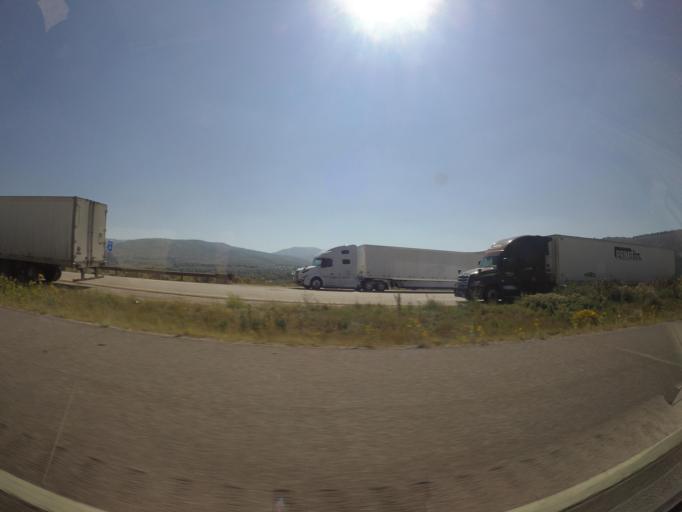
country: US
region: Colorado
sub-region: Eagle County
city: Edwards
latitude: 39.6551
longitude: -106.6098
